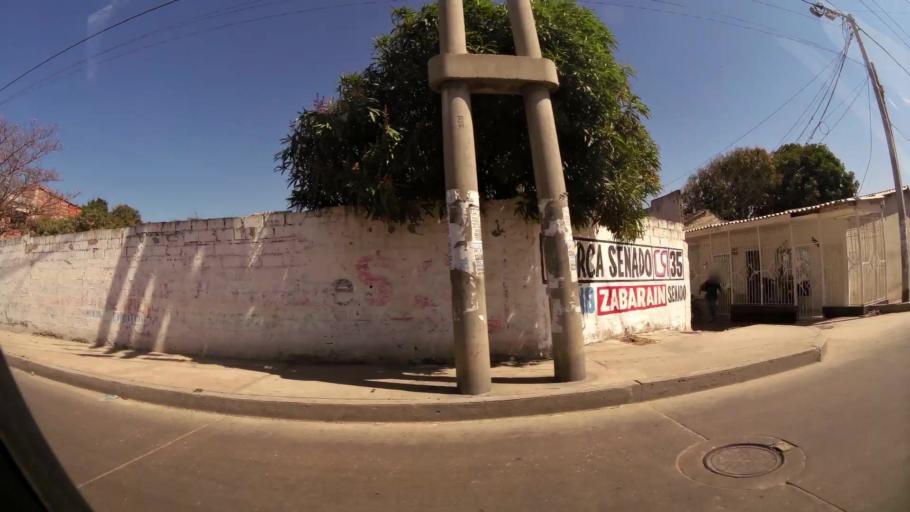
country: CO
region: Atlantico
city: Barranquilla
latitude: 10.9655
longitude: -74.7752
